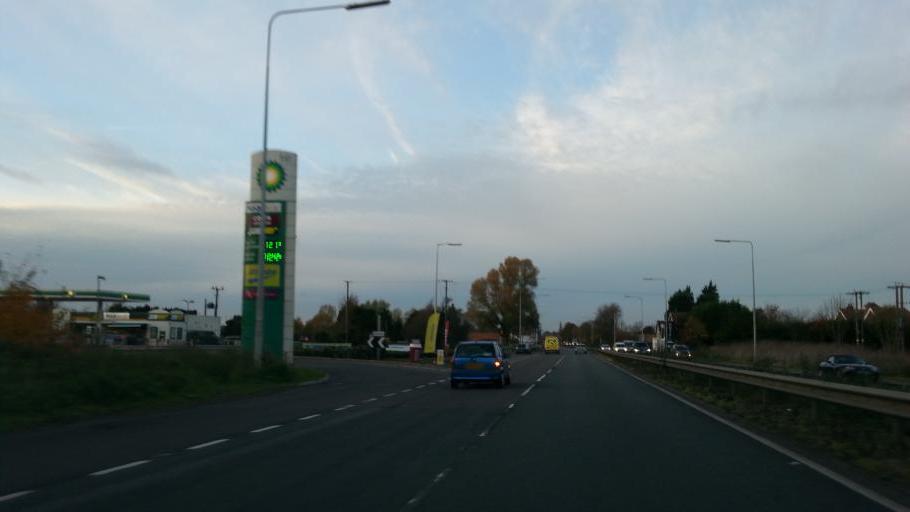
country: GB
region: England
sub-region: Central Bedfordshire
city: Astwick
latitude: 52.0281
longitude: -0.2140
